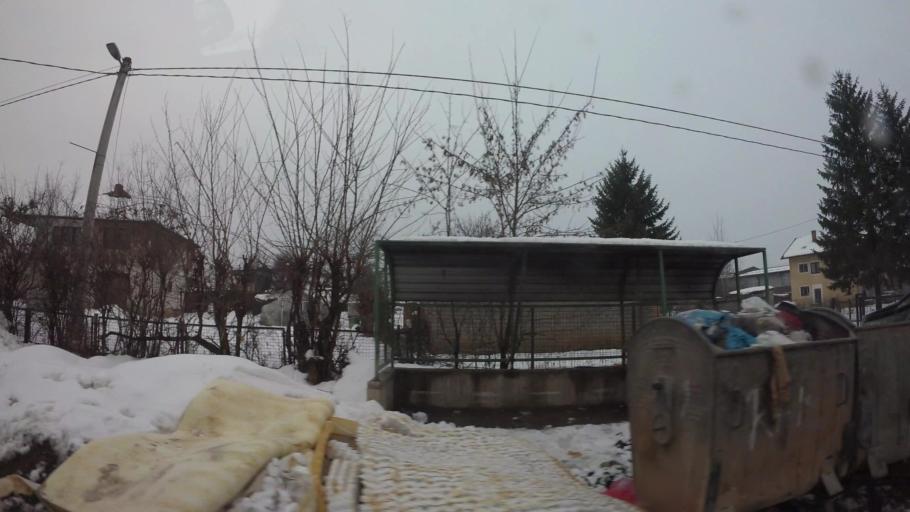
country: BA
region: Federation of Bosnia and Herzegovina
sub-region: Kanton Sarajevo
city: Sarajevo
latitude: 43.8464
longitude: 18.3168
